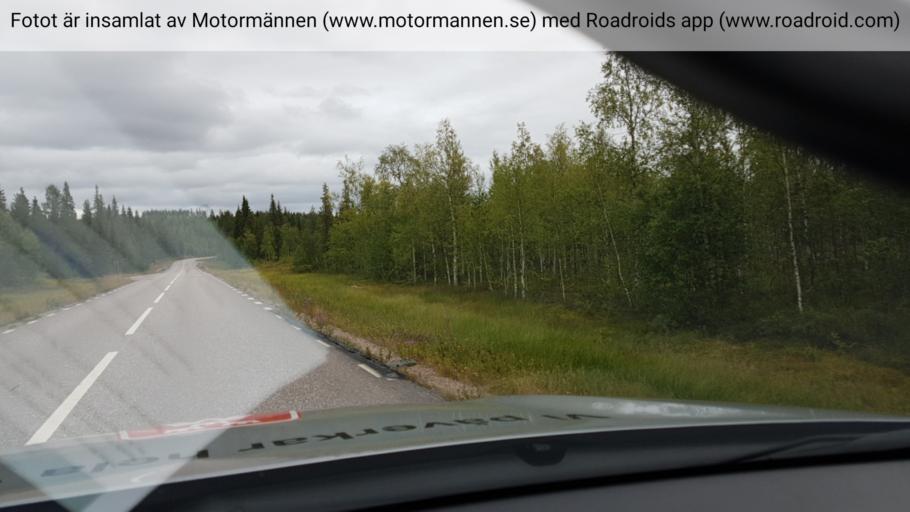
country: SE
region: Norrbotten
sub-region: Overkalix Kommun
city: OEverkalix
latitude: 67.0118
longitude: 21.9165
